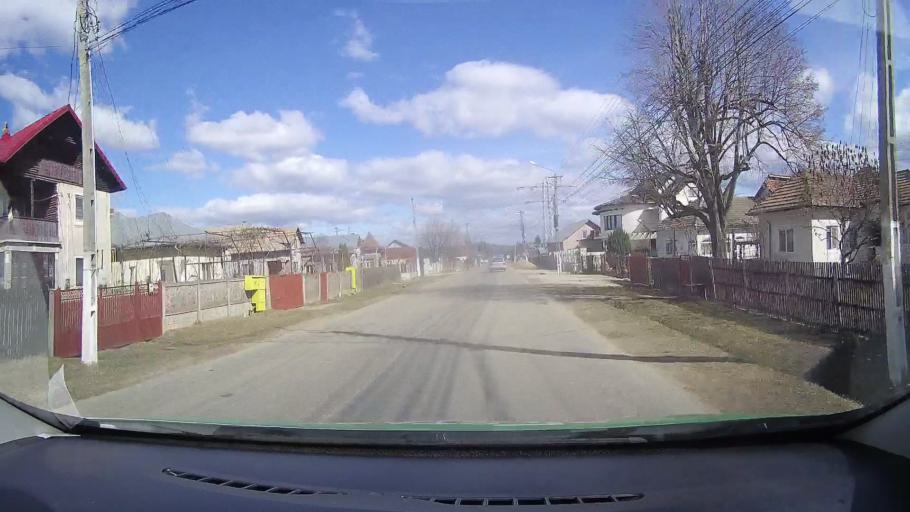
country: RO
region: Dambovita
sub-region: Comuna Vulcana-Pandele
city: Gura Vulcanei
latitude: 45.0240
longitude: 25.4025
